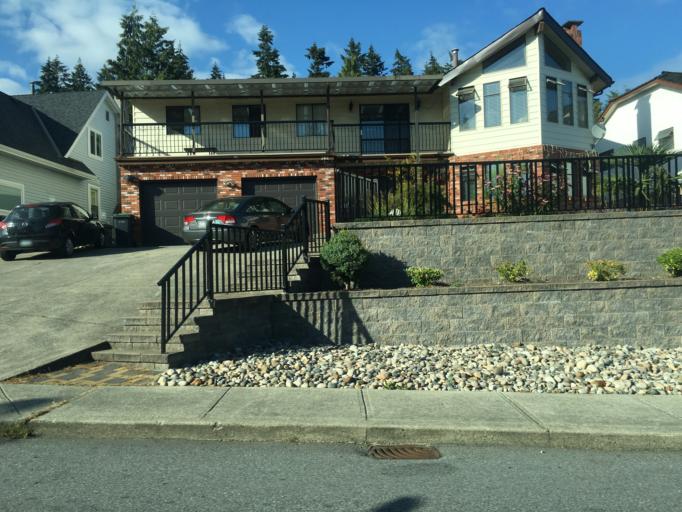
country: CA
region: British Columbia
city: Port Moody
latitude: 49.2438
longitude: -122.8232
